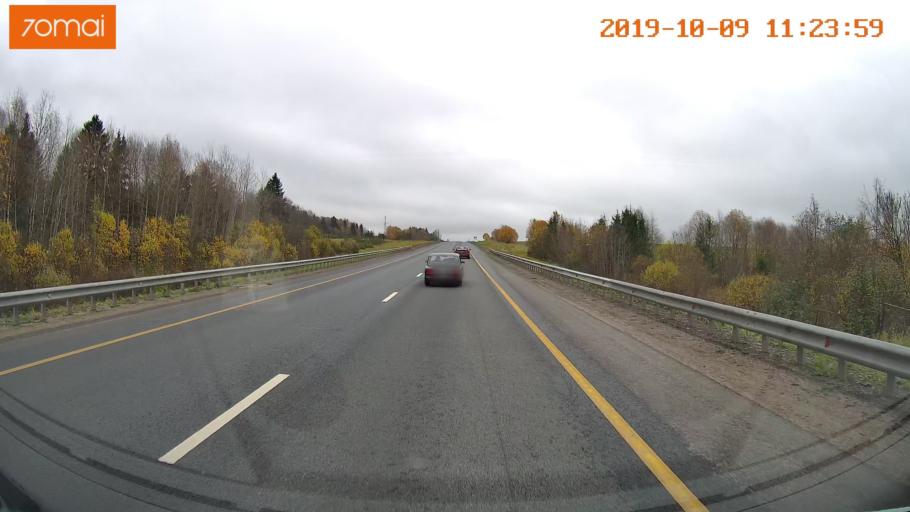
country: RU
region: Vologda
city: Vologda
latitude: 59.1155
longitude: 39.9756
